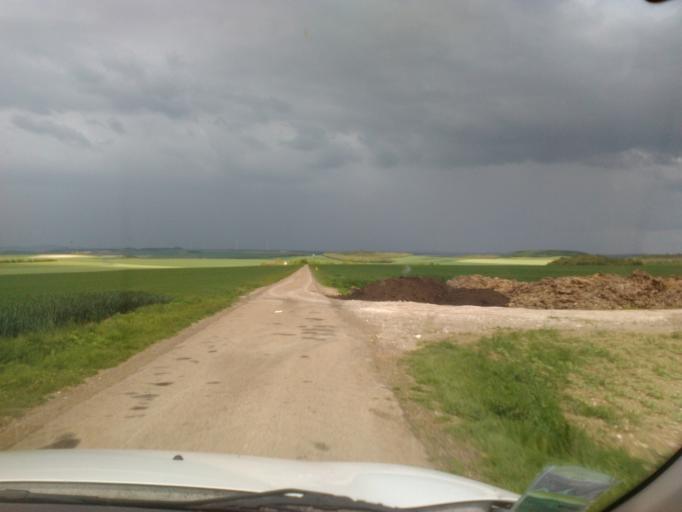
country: FR
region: Champagne-Ardenne
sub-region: Departement de l'Aube
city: Nogent-sur-Seine
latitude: 48.3778
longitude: 3.4861
